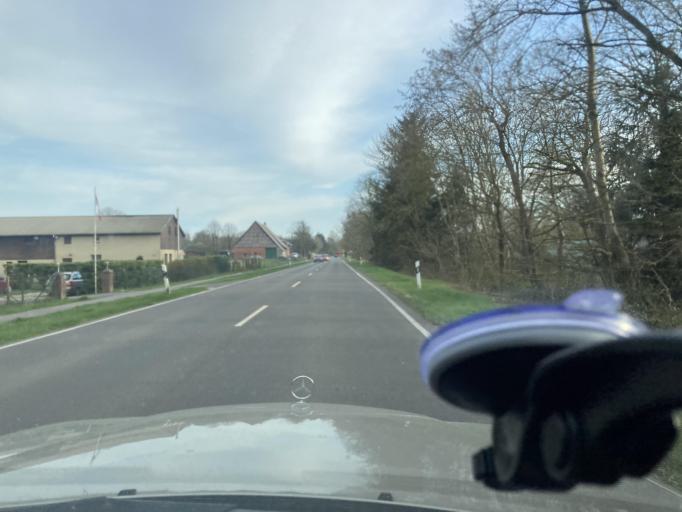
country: DE
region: Schleswig-Holstein
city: Stelle-Wittenwurth
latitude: 54.2760
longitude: 9.0467
